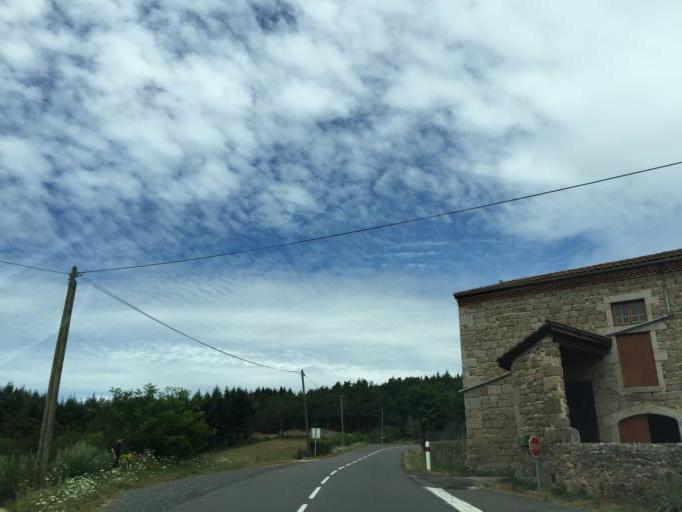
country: FR
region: Rhone-Alpes
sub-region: Departement de la Loire
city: Saint-Bonnet-le-Chateau
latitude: 45.4092
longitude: 4.1041
